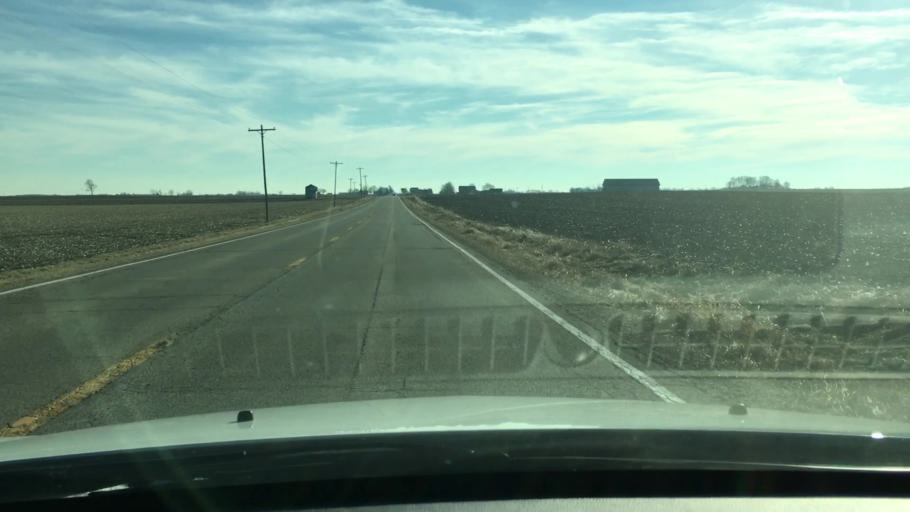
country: US
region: Illinois
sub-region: LaSalle County
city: Mendota
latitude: 41.4940
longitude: -89.1272
